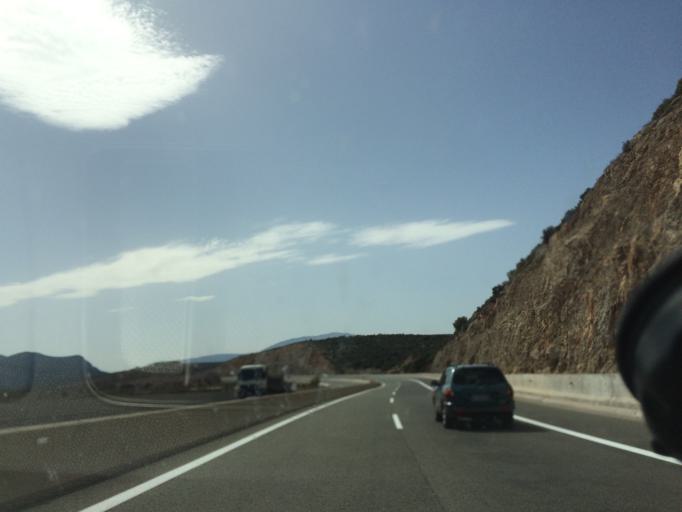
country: GR
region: Central Greece
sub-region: Nomos Voiotias
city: Akraifnia
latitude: 38.4206
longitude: 23.2194
